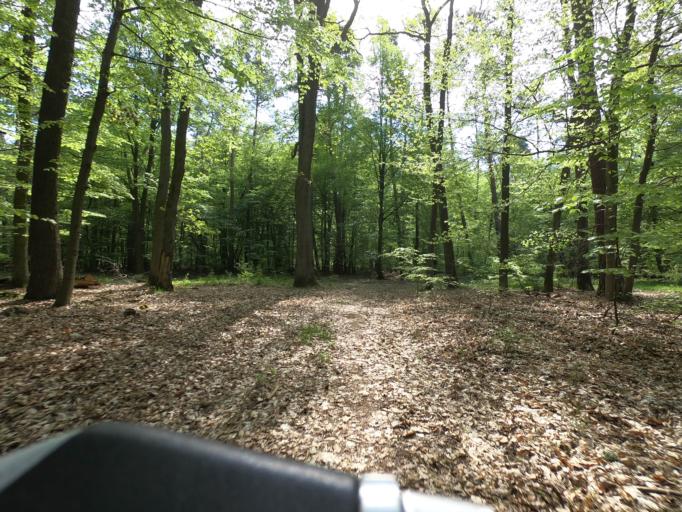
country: DE
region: Hesse
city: Morfelden-Walldorf
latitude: 50.0214
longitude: 8.5692
